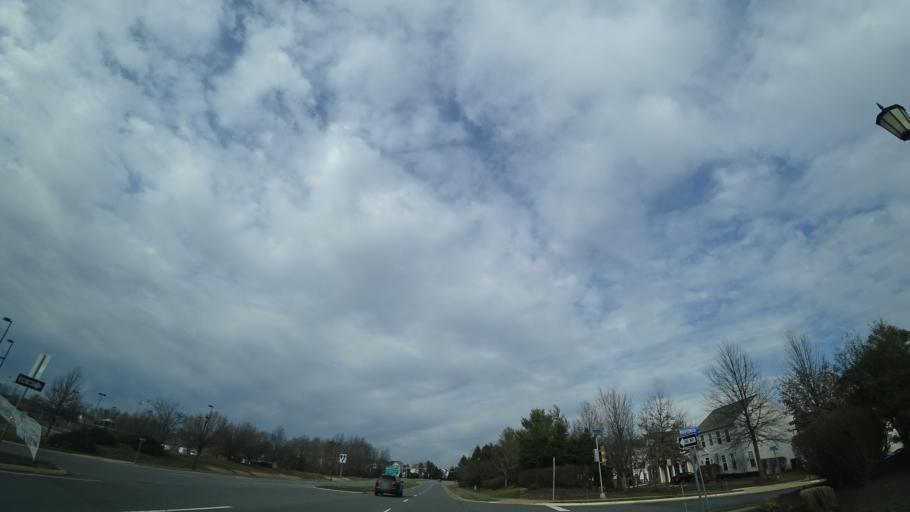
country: US
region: Virginia
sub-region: Loudoun County
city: Belmont
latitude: 39.0483
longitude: -77.5069
